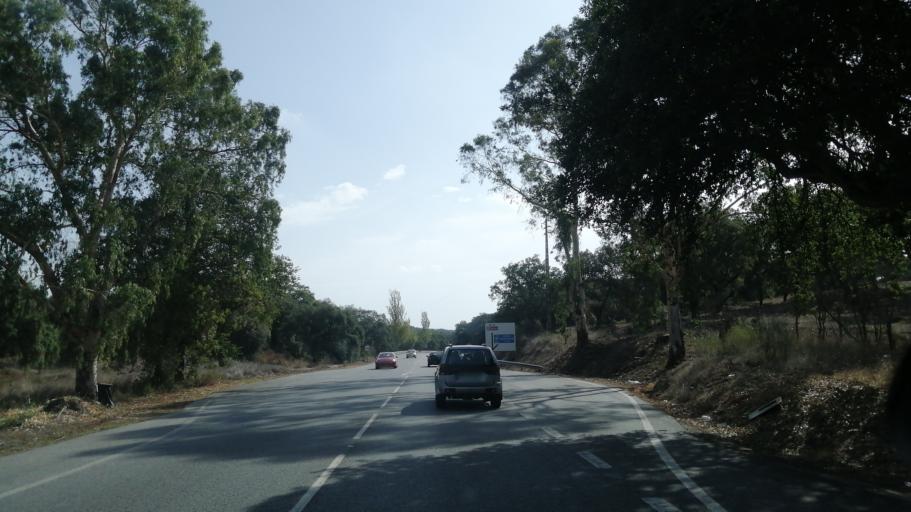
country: PT
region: Evora
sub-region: Arraiolos
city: Arraiolos
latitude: 38.5994
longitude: -8.0308
